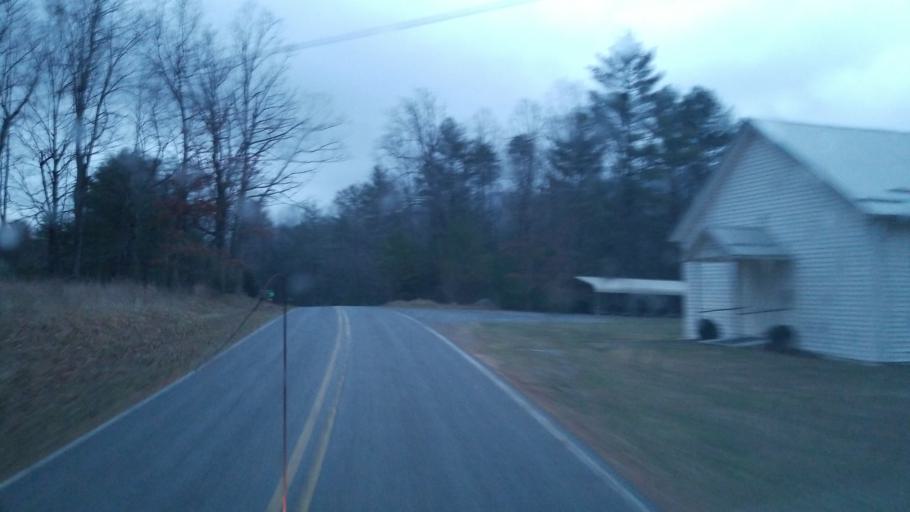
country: US
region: Virginia
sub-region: Pulaski County
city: Pulaski
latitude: 37.1146
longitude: -80.8793
